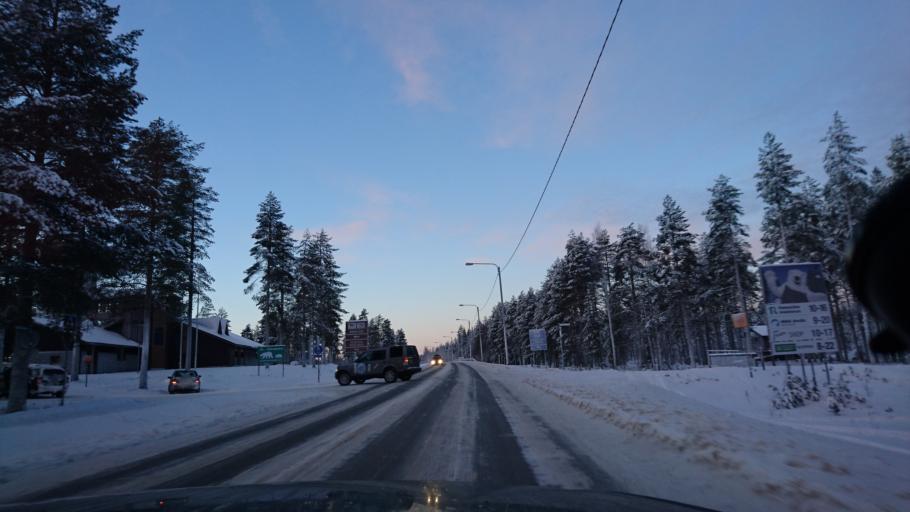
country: FI
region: Lapland
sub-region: Rovaniemi
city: Ranua
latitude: 65.9439
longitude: 26.4691
